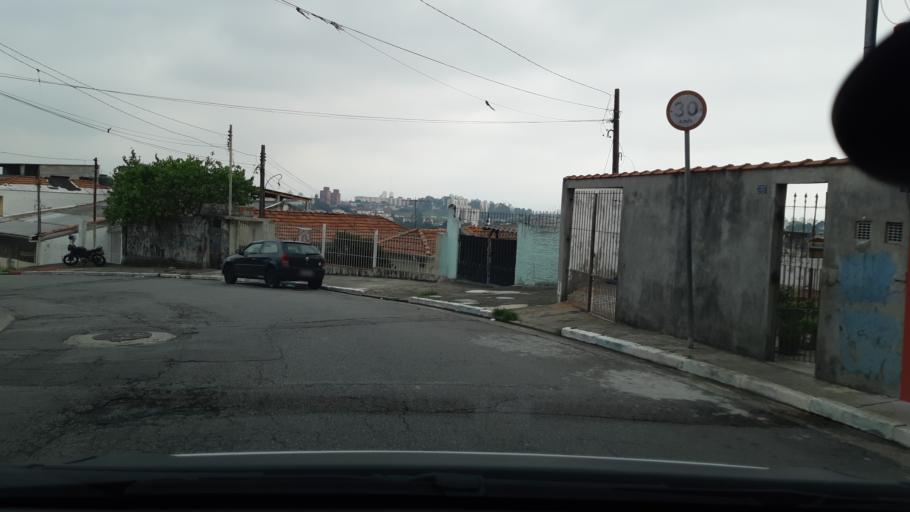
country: BR
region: Sao Paulo
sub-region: Sao Caetano Do Sul
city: Sao Caetano do Sul
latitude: -23.6335
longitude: -46.6037
